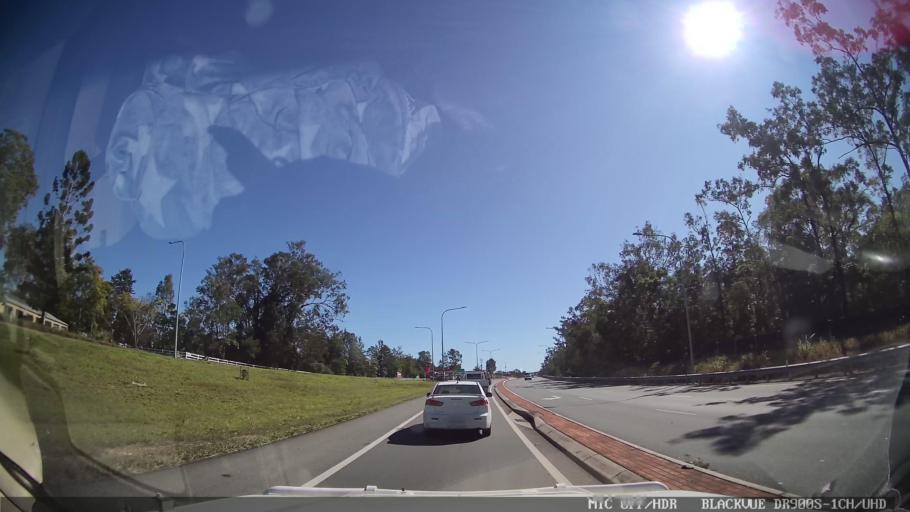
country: AU
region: Queensland
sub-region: Gympie Regional Council
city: Monkland
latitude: -26.2403
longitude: 152.7003
